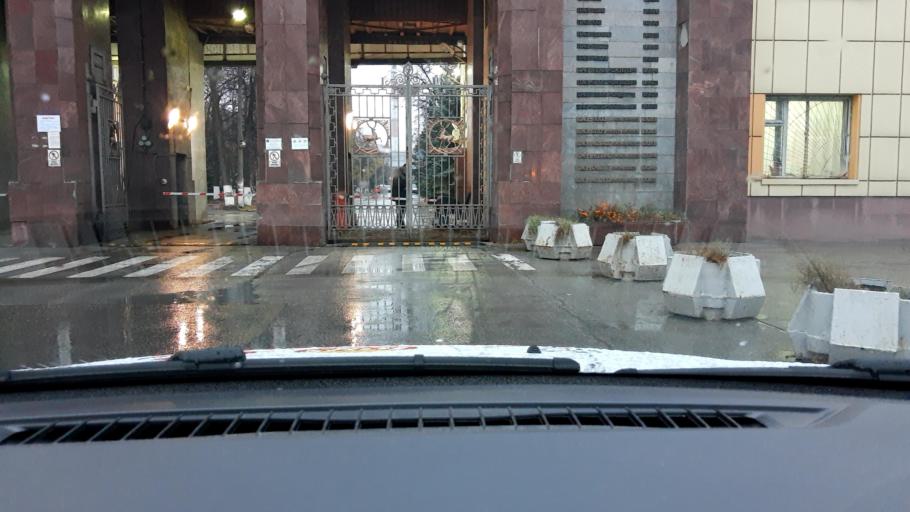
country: RU
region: Nizjnij Novgorod
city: Gorbatovka
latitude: 56.2482
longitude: 43.8817
